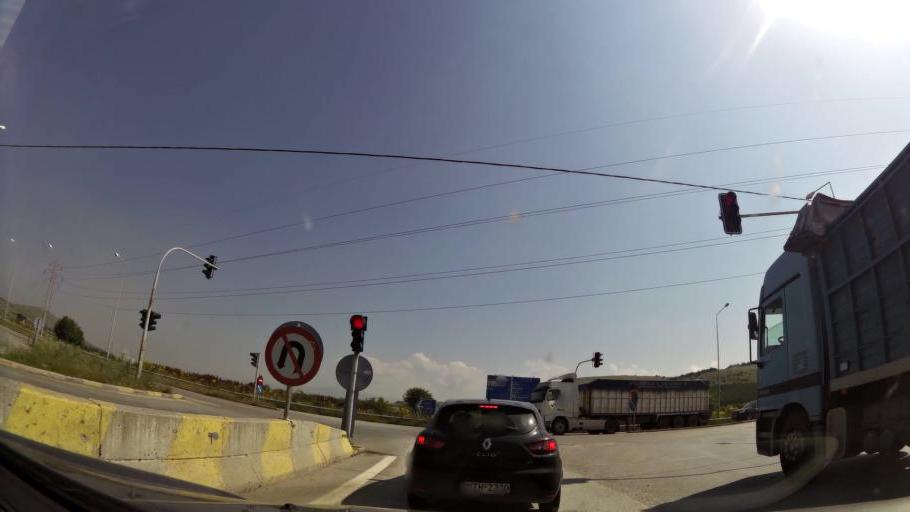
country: GR
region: West Macedonia
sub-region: Nomos Kozanis
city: Koila
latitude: 40.3424
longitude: 21.8103
